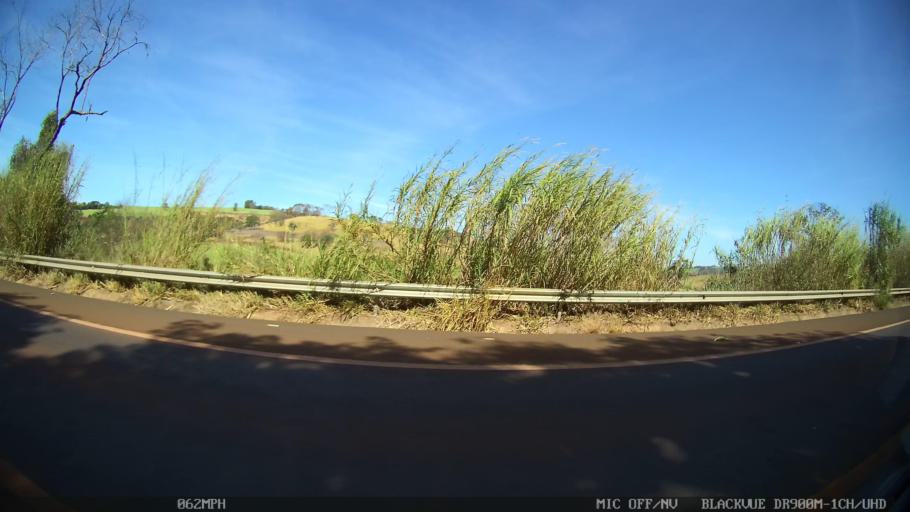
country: BR
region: Sao Paulo
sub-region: Sao Joaquim Da Barra
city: Sao Joaquim da Barra
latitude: -20.5533
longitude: -47.6735
